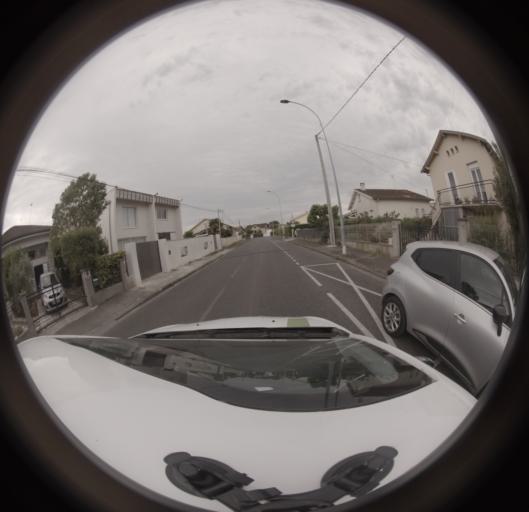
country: FR
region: Midi-Pyrenees
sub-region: Departement du Tarn-et-Garonne
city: Montauban
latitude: 44.0192
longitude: 1.3743
